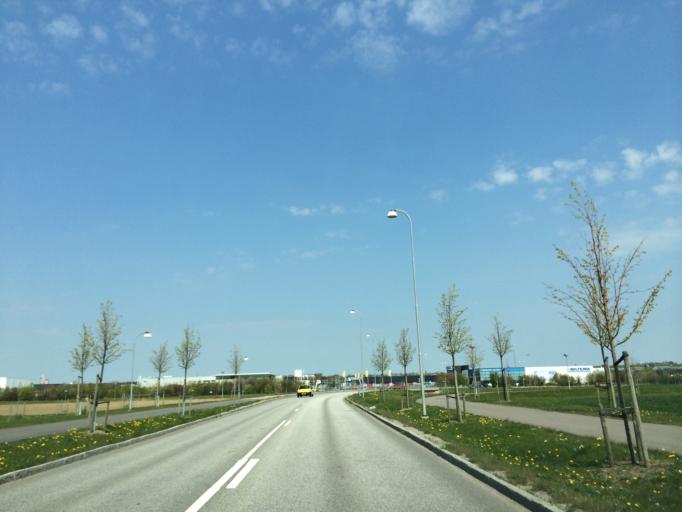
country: SE
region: Skane
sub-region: Lunds Kommun
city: Lund
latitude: 55.6857
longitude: 13.2148
